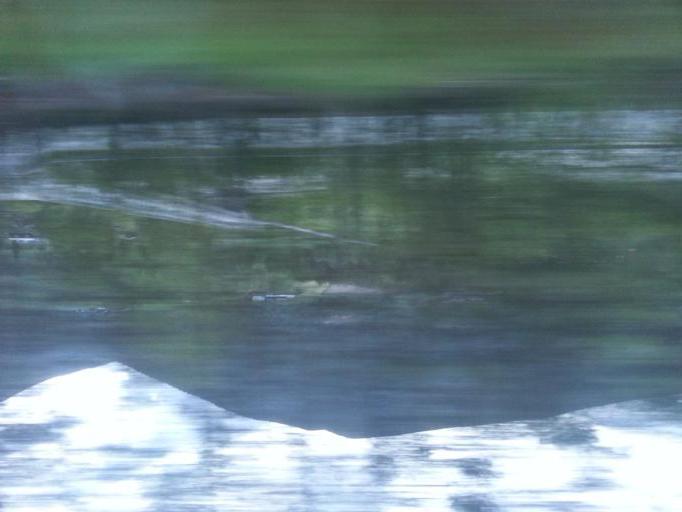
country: NO
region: Oppland
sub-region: Dovre
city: Dovre
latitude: 61.9275
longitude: 9.3135
